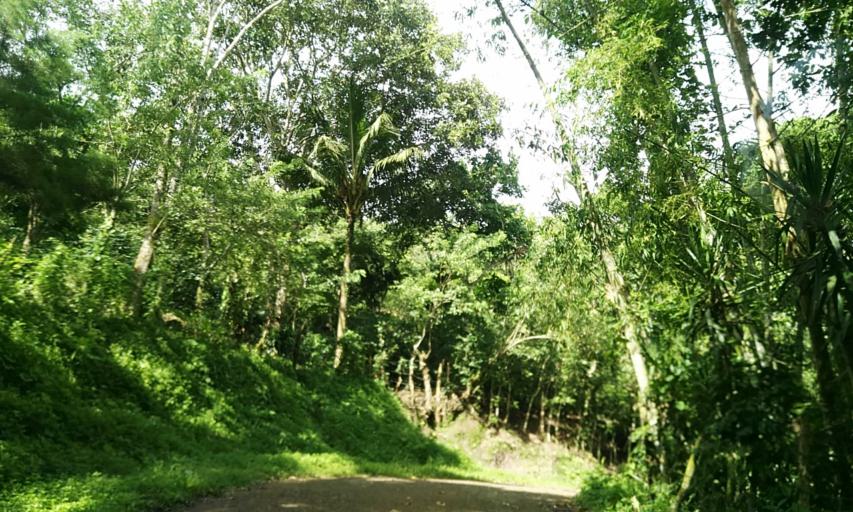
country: NI
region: Matagalpa
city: San Ramon
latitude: 12.9906
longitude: -85.8570
